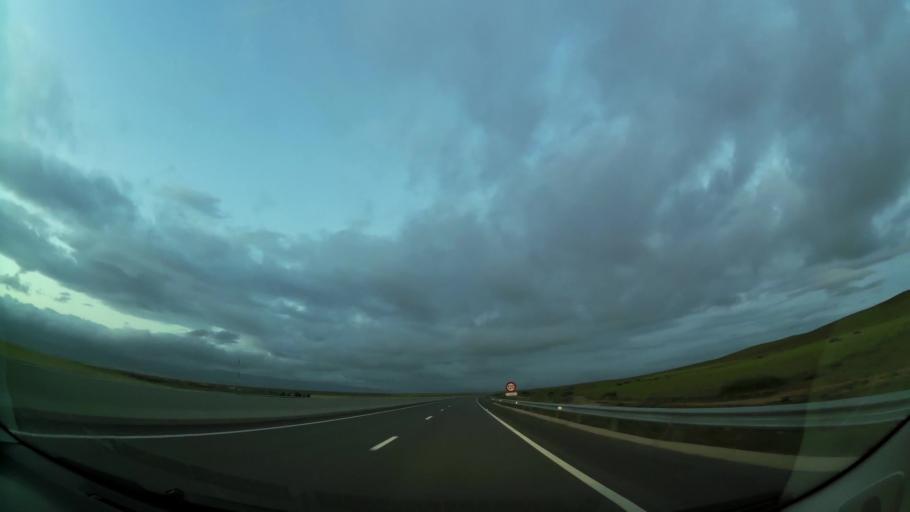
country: MA
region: Oriental
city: El Aioun
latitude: 34.6244
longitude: -2.3914
